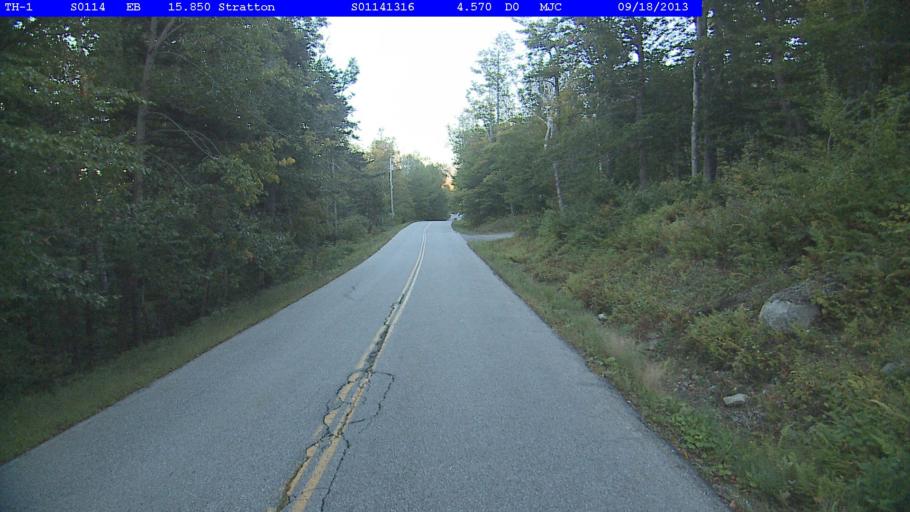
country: US
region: Vermont
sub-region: Windham County
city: Dover
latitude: 43.0482
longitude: -72.9208
